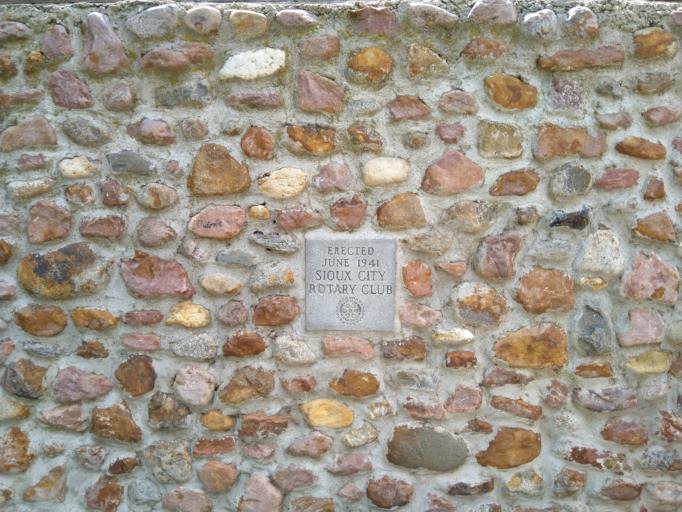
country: US
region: South Dakota
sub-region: Union County
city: North Sioux City
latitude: 42.5509
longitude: -96.4682
